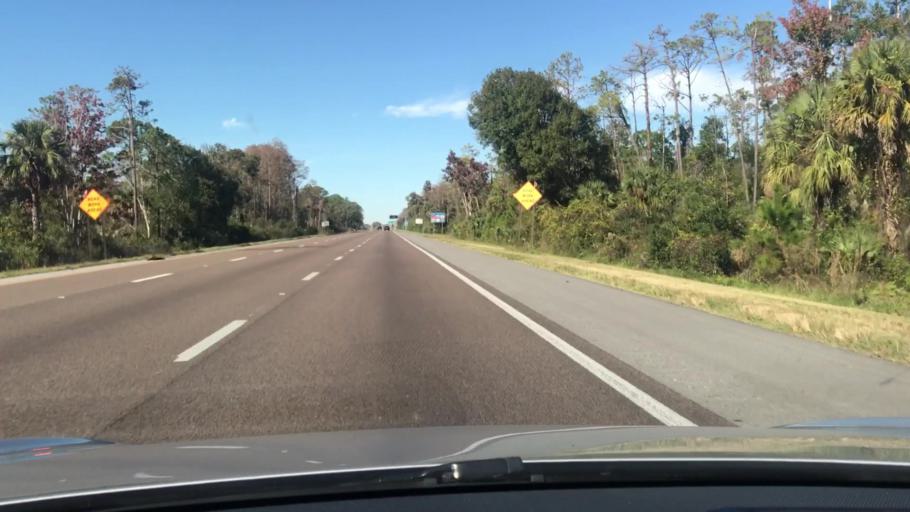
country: US
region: Florida
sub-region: Volusia County
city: Glencoe
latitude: 29.0003
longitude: -80.9794
